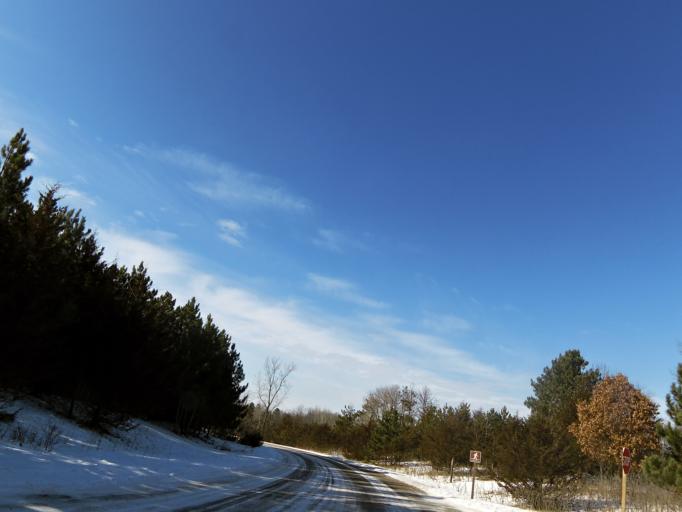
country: US
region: Wisconsin
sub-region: Saint Croix County
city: North Hudson
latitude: 45.0134
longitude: -92.6802
